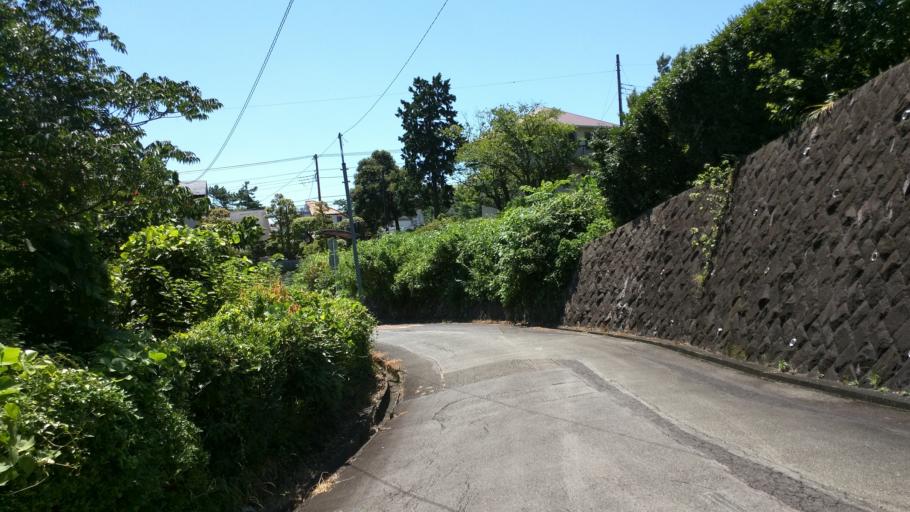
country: JP
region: Shizuoka
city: Ito
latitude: 34.8885
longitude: 139.1214
